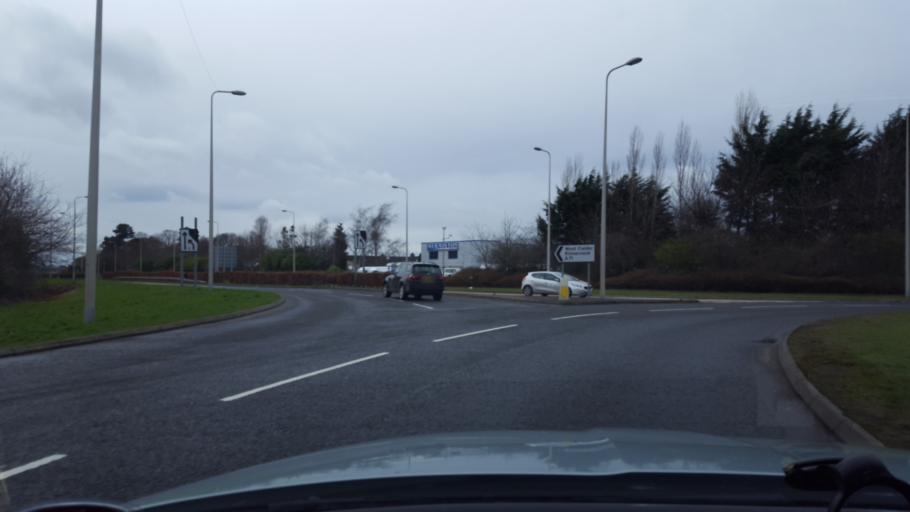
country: GB
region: Scotland
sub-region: Edinburgh
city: Currie
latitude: 55.9176
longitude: -3.3135
